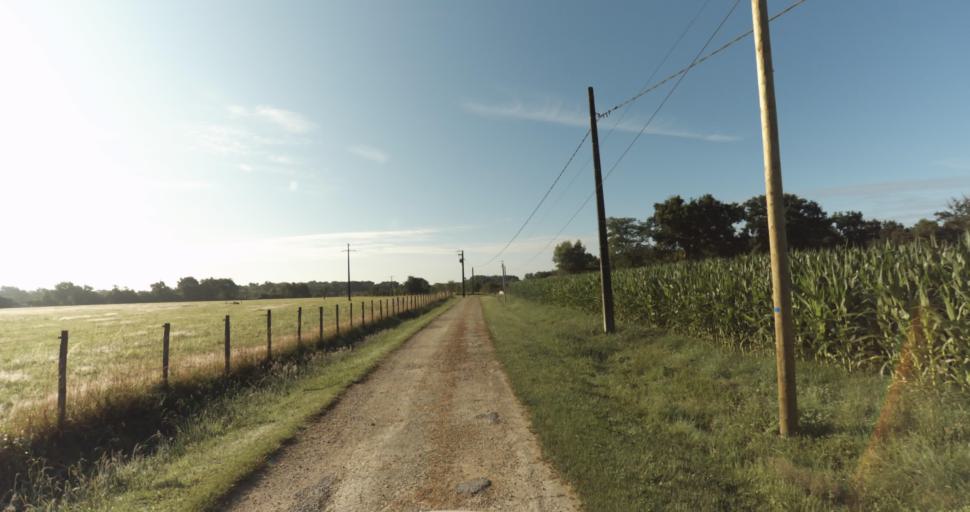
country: FR
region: Aquitaine
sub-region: Departement de la Gironde
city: Bazas
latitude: 44.4118
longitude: -0.2200
